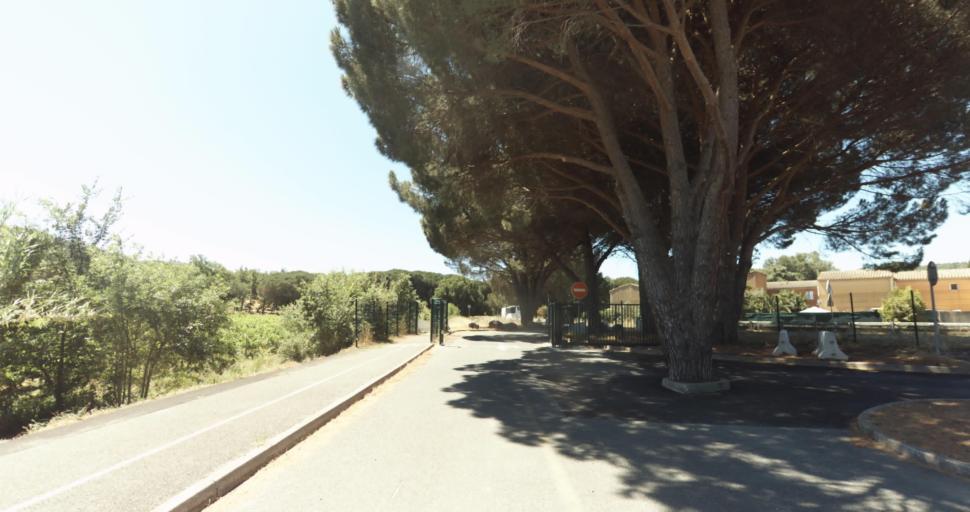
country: FR
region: Provence-Alpes-Cote d'Azur
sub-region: Departement du Var
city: Gassin
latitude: 43.2451
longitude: 6.5732
